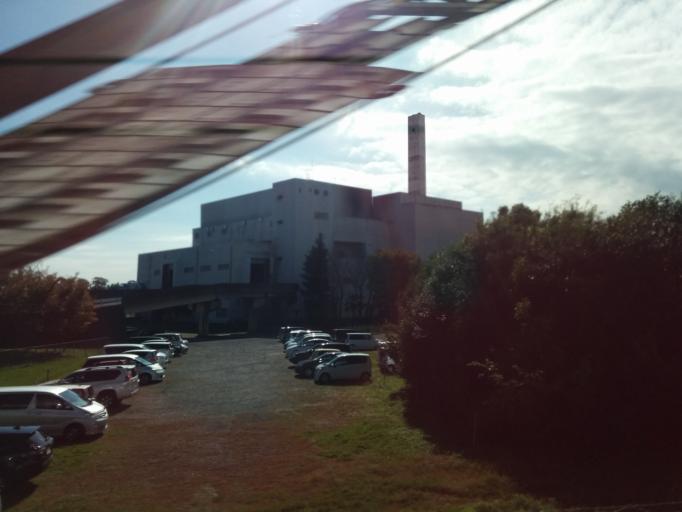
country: JP
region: Kanagawa
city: Atsugi
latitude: 35.4035
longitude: 139.4016
